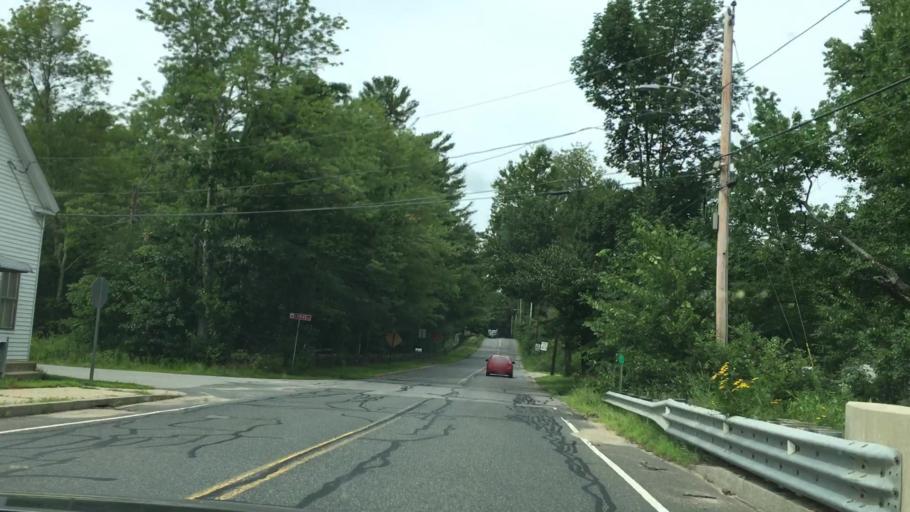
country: US
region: Massachusetts
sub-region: Worcester County
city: Winchendon
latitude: 42.6954
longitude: -72.0150
